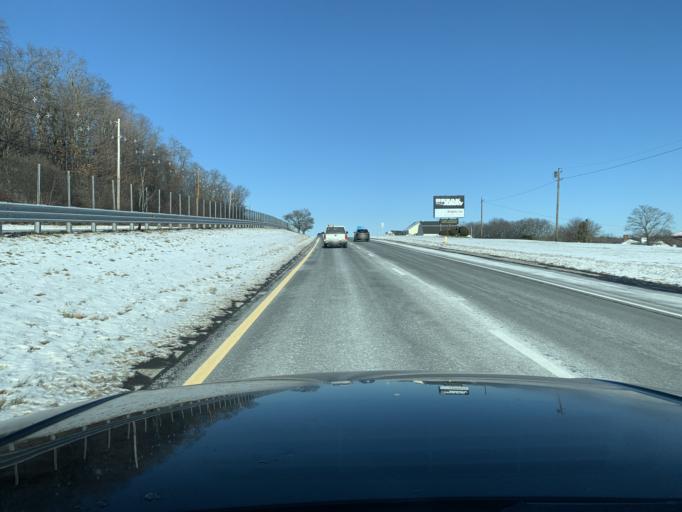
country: US
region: Massachusetts
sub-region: Essex County
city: Danvers
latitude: 42.5778
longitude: -70.9699
